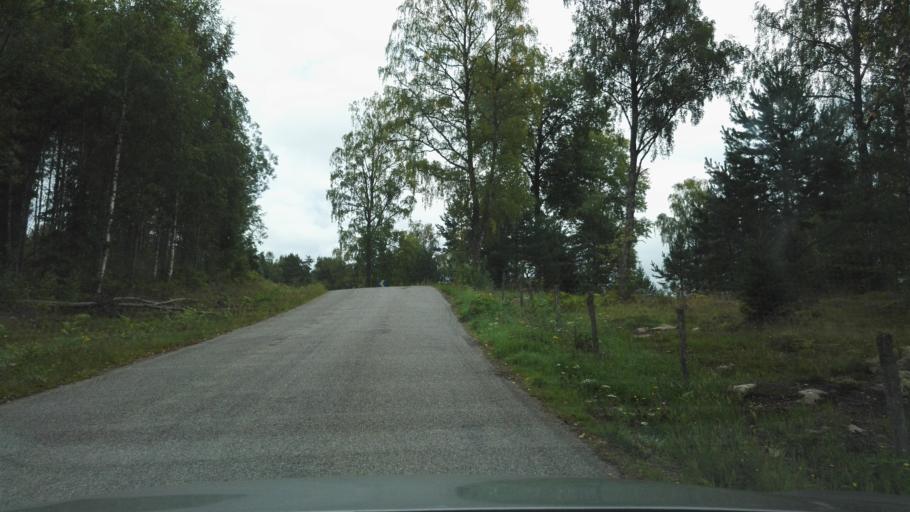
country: SE
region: Joenkoeping
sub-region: Vetlanda Kommun
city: Landsbro
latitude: 57.2231
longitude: 14.8168
